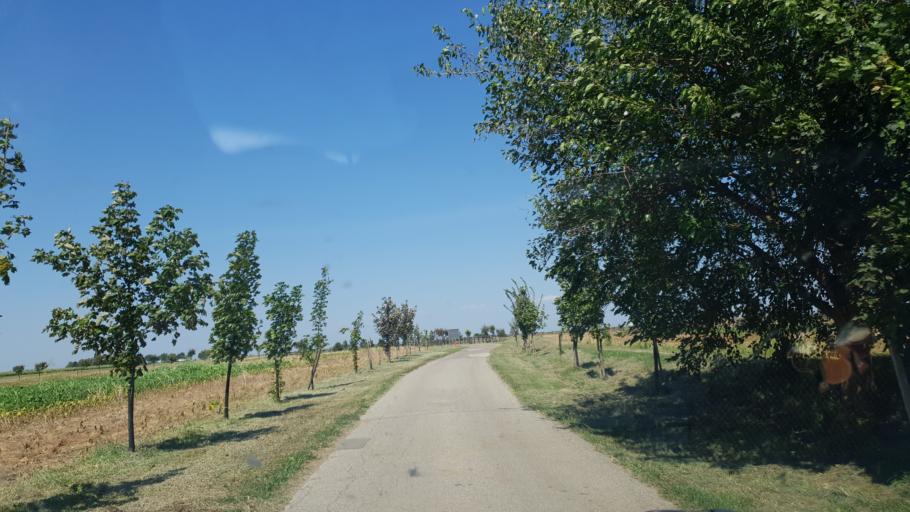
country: RS
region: Autonomna Pokrajina Vojvodina
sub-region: Juznobacki Okrug
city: Kovilj
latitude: 45.2083
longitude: 20.0630
